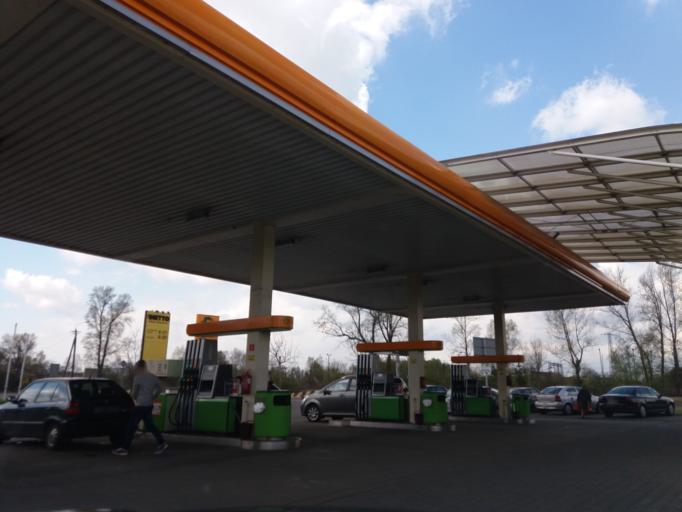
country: PL
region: Lesser Poland Voivodeship
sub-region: Powiat oswiecimski
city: Oswiecim
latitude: 50.0487
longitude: 19.2138
